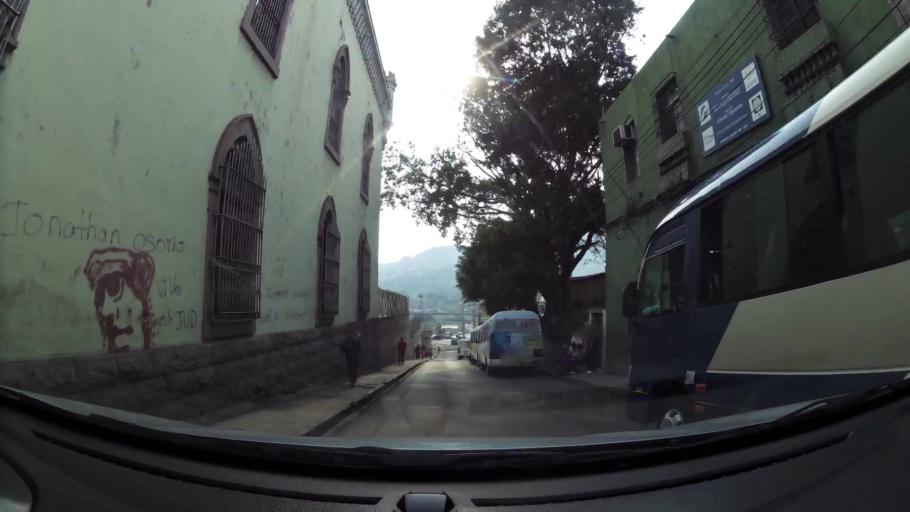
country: HN
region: Francisco Morazan
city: Tegucigalpa
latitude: 14.1043
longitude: -87.2062
